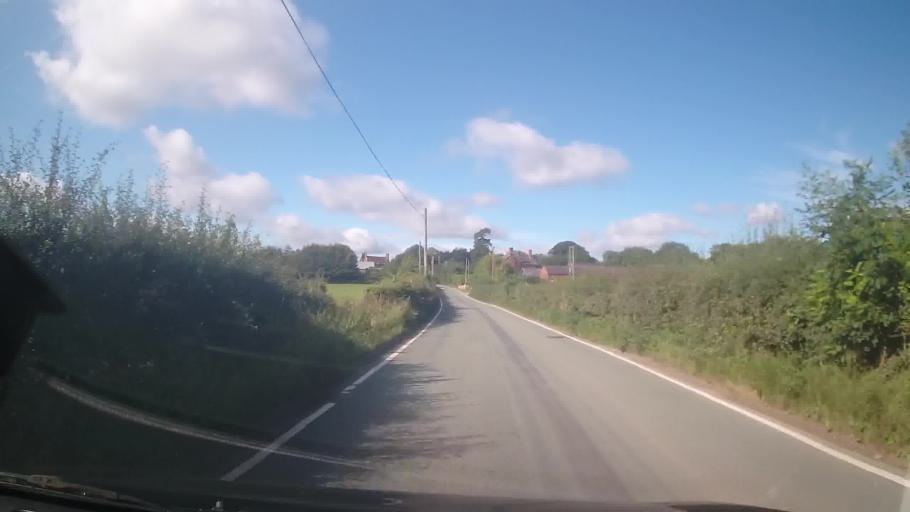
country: GB
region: England
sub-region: Shropshire
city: Bicton
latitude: 52.7632
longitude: -2.7875
